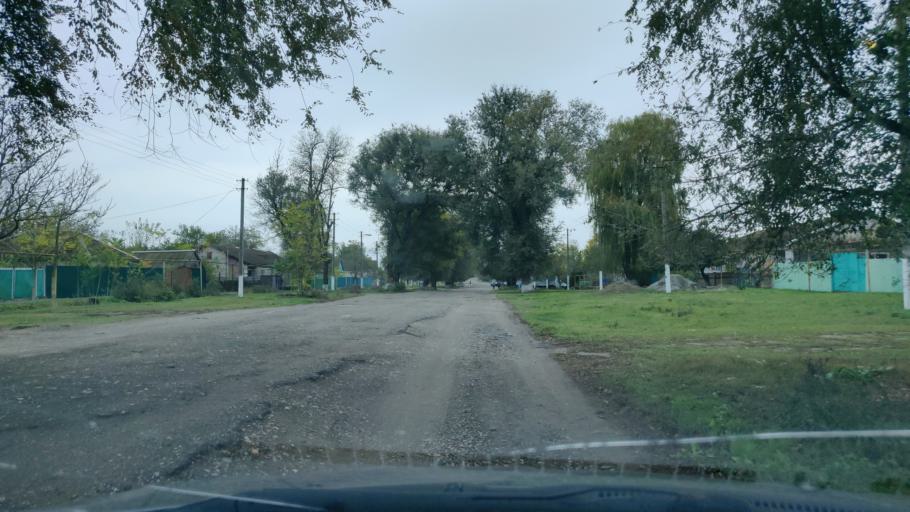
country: RU
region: Stavropol'skiy
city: Irgakly
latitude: 44.2414
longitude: 44.7220
